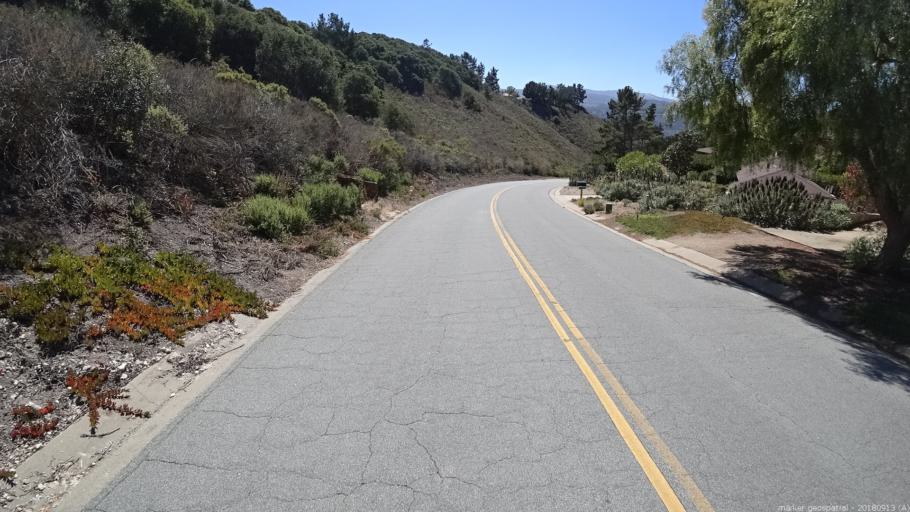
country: US
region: California
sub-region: Monterey County
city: Carmel Valley Village
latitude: 36.5357
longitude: -121.7990
